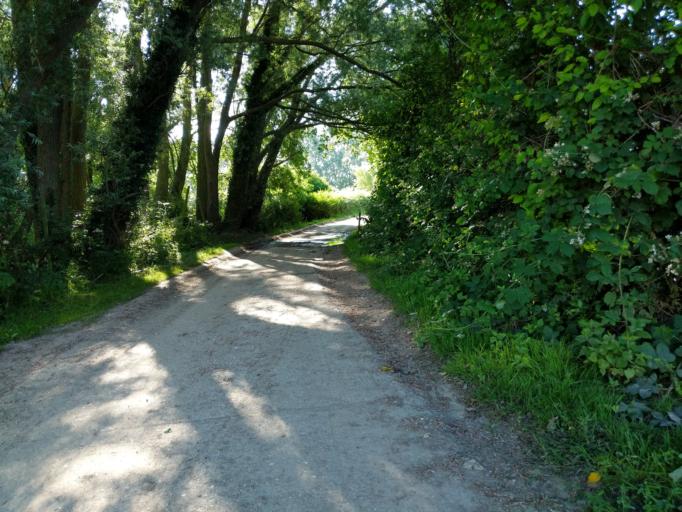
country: GB
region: England
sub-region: Kent
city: Faversham
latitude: 51.3299
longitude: 0.9298
